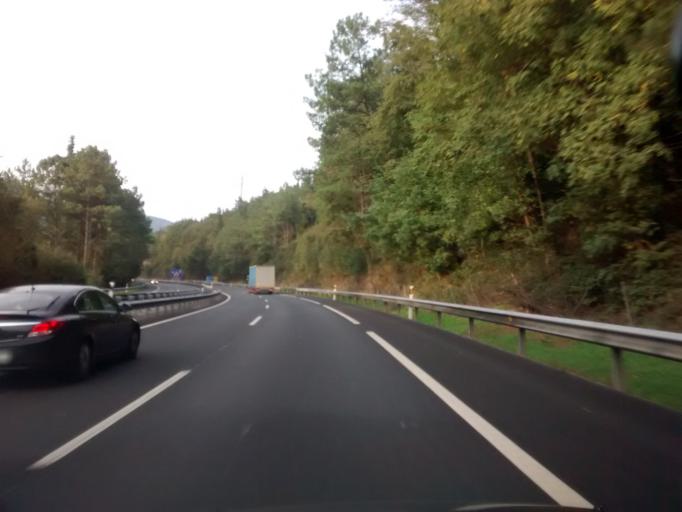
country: ES
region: Basque Country
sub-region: Provincia de Guipuzcoa
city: Elgoibar
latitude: 43.2206
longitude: -2.4031
